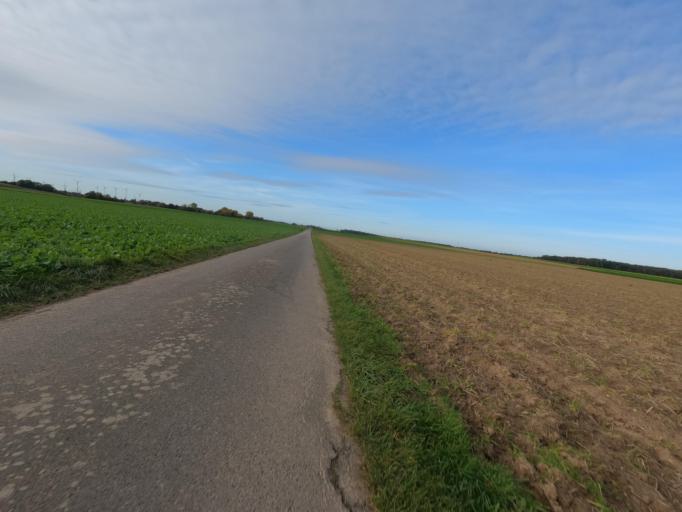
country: DE
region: North Rhine-Westphalia
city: Erkelenz
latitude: 51.0423
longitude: 6.3473
